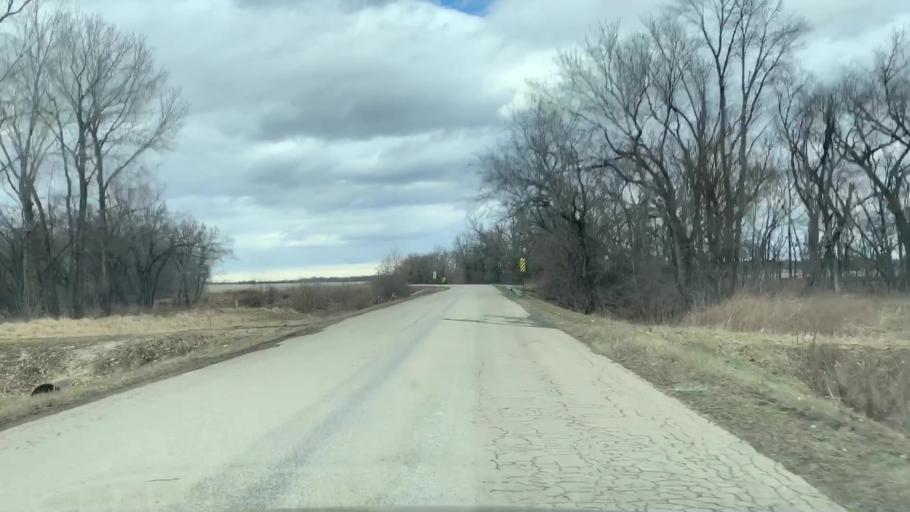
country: US
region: Kansas
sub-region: Allen County
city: Humboldt
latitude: 37.8093
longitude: -95.4708
